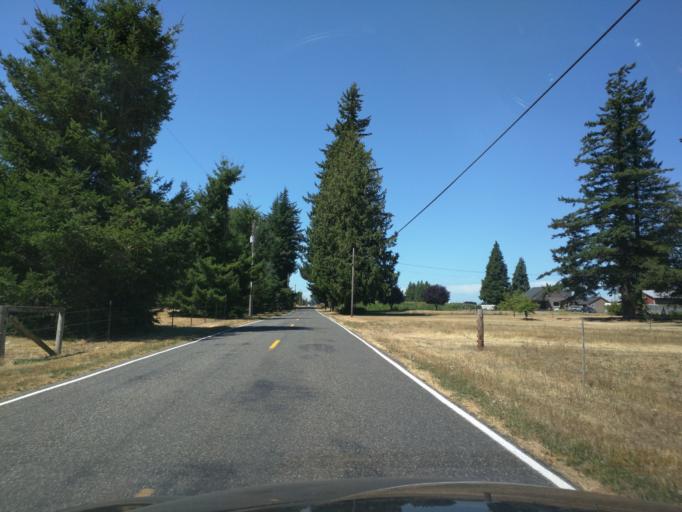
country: US
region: Washington
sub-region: Whatcom County
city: Lynden
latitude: 48.8772
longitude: -122.4273
